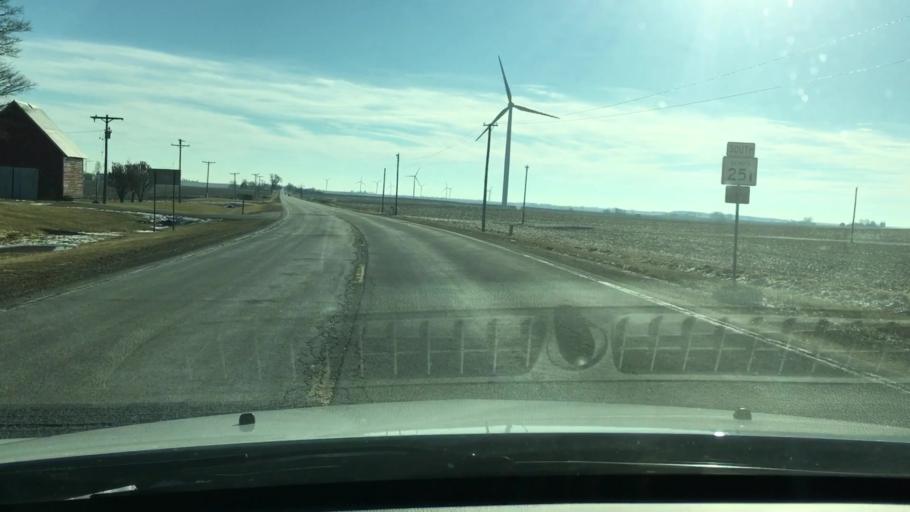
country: US
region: Illinois
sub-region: LaSalle County
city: Mendota
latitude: 41.6810
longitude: -89.1298
